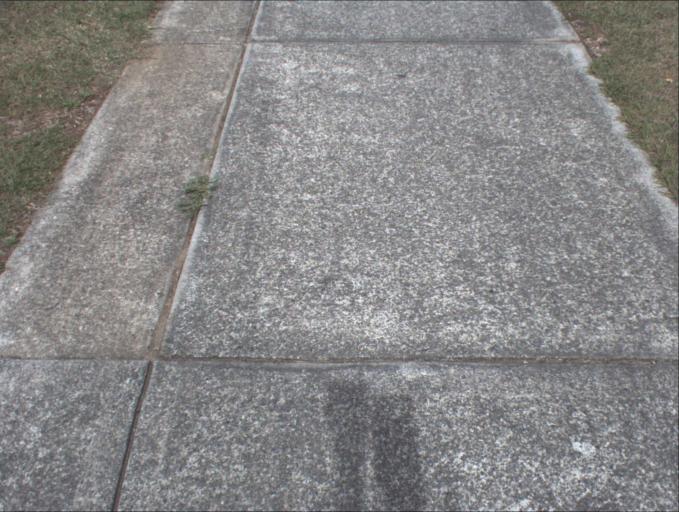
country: AU
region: Queensland
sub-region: Logan
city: Beenleigh
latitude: -27.7082
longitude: 153.2003
